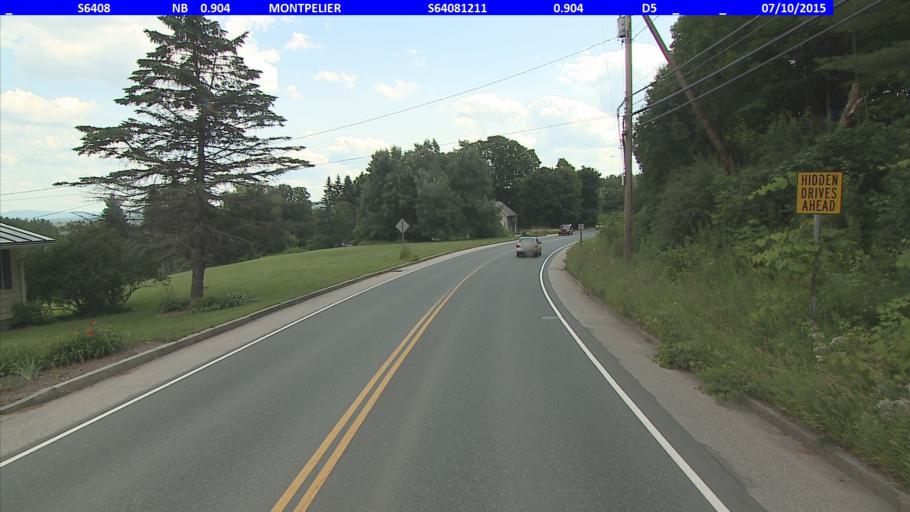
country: US
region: Vermont
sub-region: Washington County
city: Montpelier
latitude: 44.2401
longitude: -72.5631
